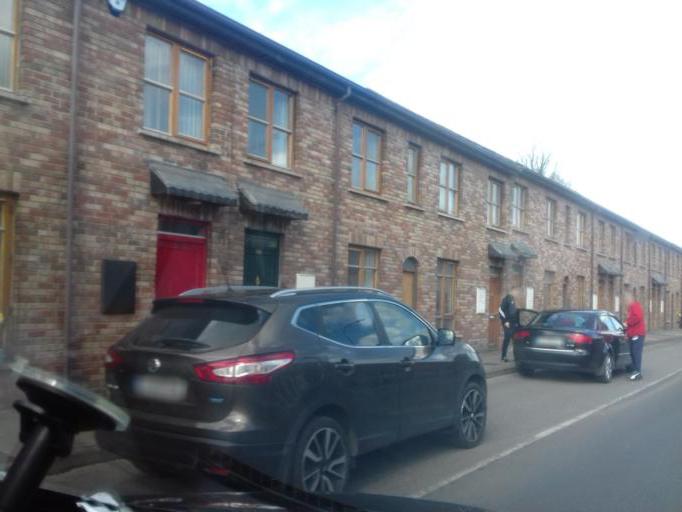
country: IE
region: Ulster
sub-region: An Cabhan
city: Cavan
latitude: 53.9886
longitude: -7.3620
